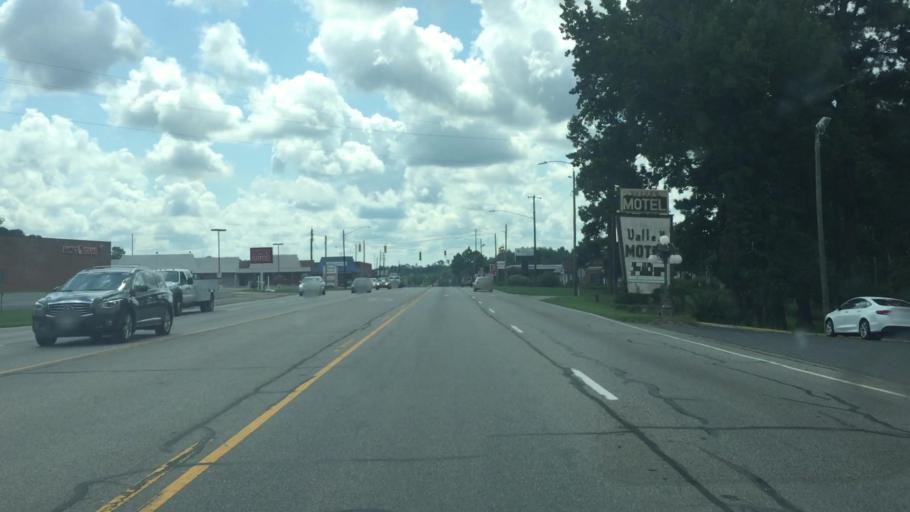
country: US
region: North Carolina
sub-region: Anson County
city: Wadesboro
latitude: 34.9678
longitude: -80.0643
